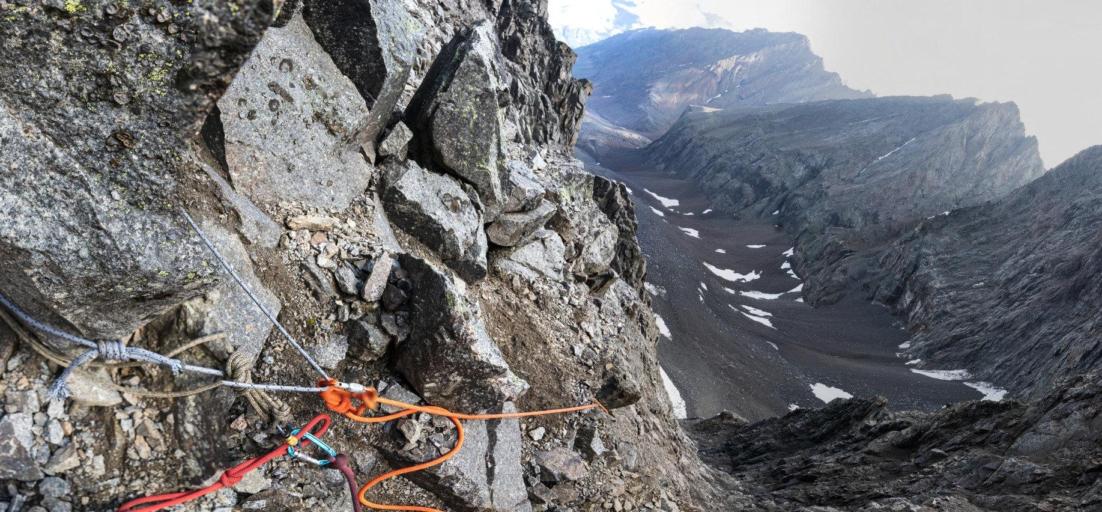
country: RU
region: Transbaikal Territory
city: Chara
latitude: 56.8785
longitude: 117.6695
